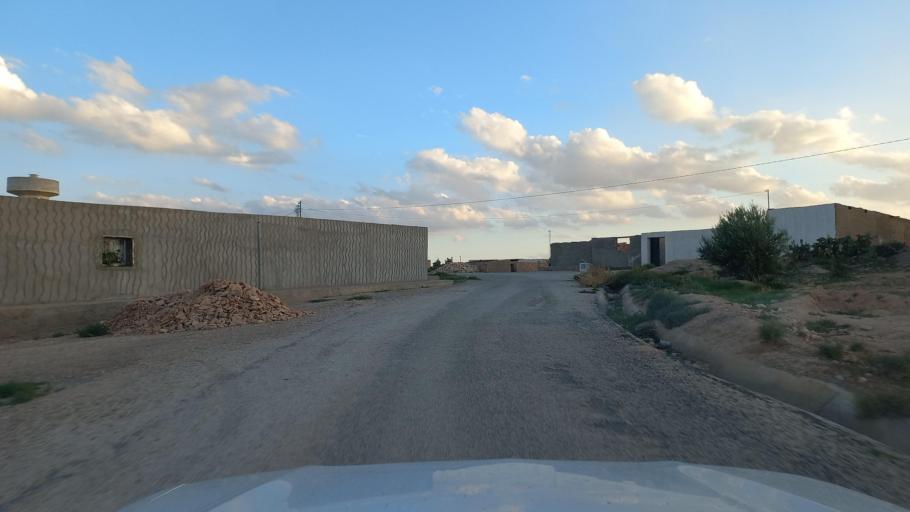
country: TN
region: Al Qasrayn
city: Sbiba
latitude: 35.3734
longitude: 9.0619
